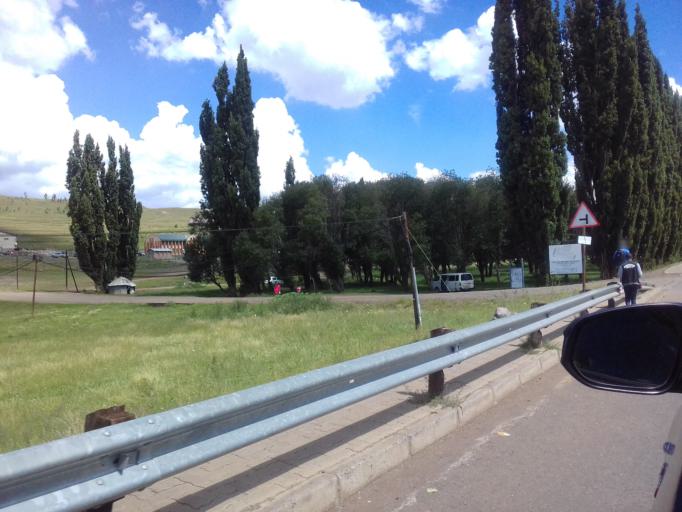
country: LS
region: Thaba-Tseka
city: Thaba-Tseka
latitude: -29.5221
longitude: 28.6031
